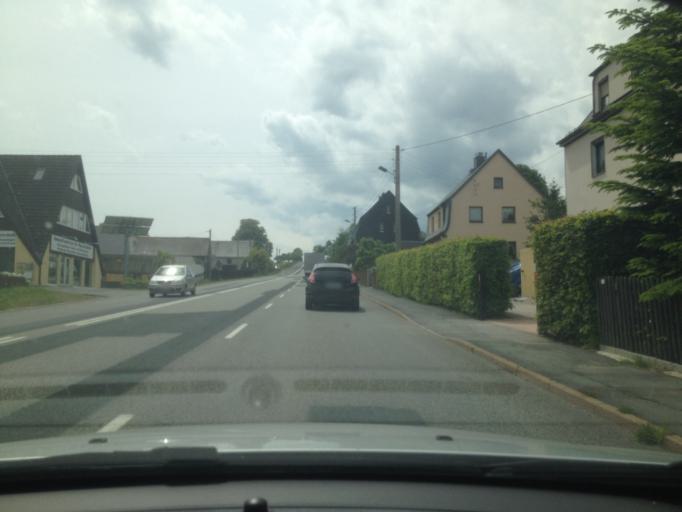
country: DE
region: Saxony
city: Stollberg
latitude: 50.6678
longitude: 12.7620
